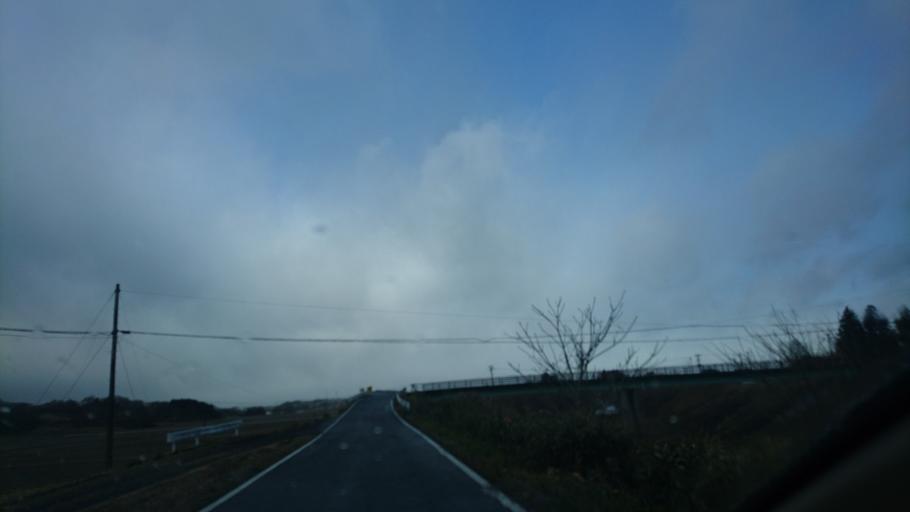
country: JP
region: Iwate
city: Ichinoseki
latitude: 38.7719
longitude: 141.0301
